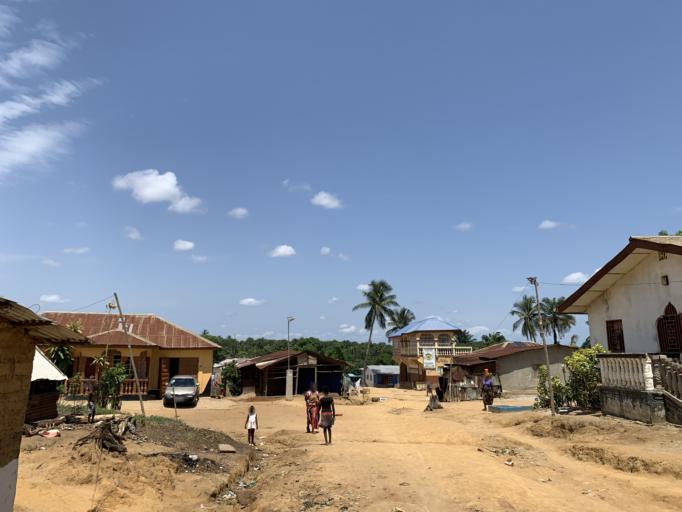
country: SL
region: Western Area
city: Waterloo
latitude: 8.3230
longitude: -13.0616
